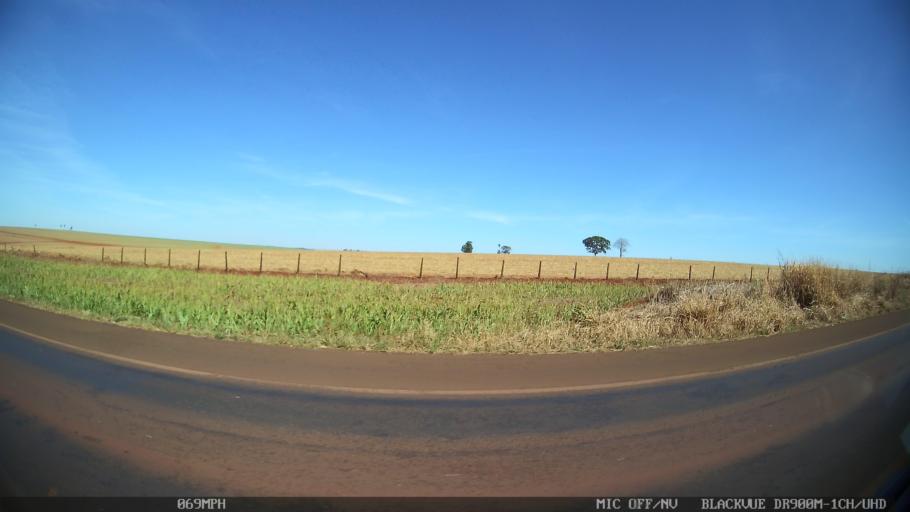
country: BR
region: Sao Paulo
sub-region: Sao Joaquim Da Barra
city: Sao Joaquim da Barra
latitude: -20.5086
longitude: -47.9173
